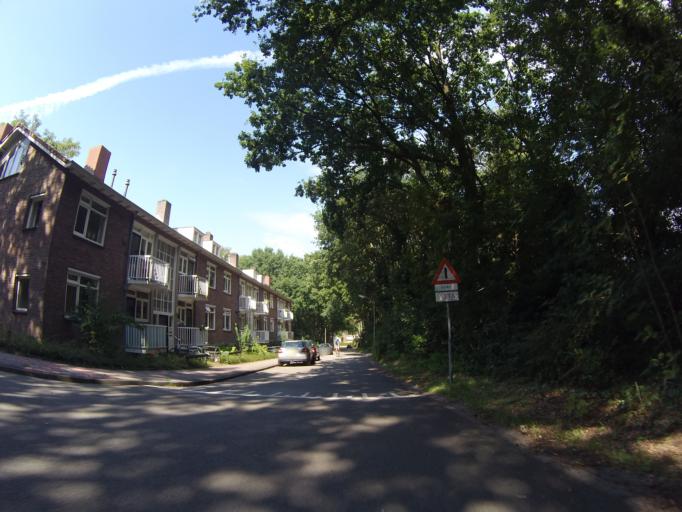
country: NL
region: Utrecht
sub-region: Gemeente Amersfoort
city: Amersfoort
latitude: 52.1482
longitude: 5.3607
